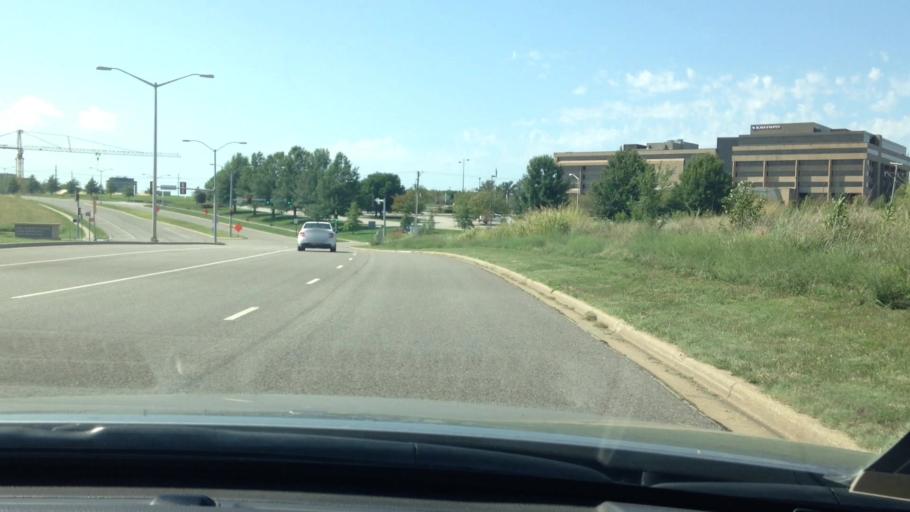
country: US
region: Kansas
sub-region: Johnson County
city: Leawood
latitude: 38.9215
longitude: -94.6530
